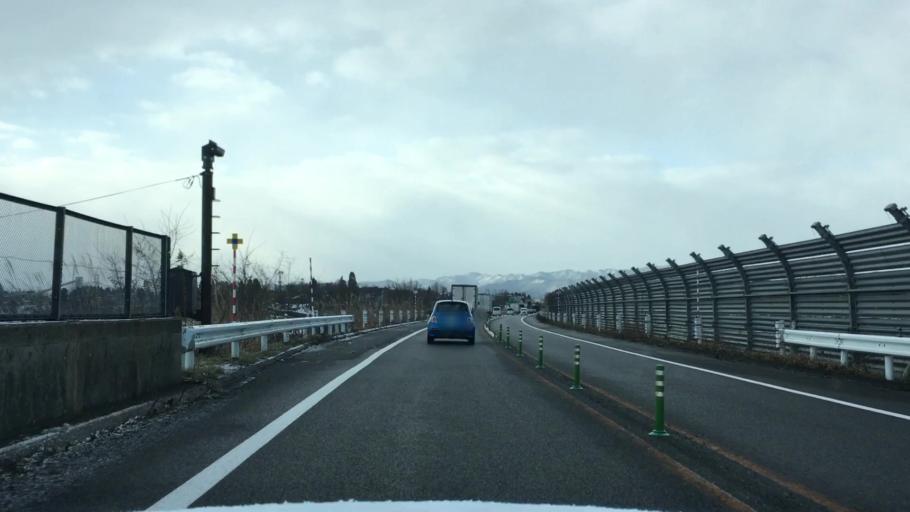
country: JP
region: Akita
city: Odate
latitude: 40.2820
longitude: 140.5397
